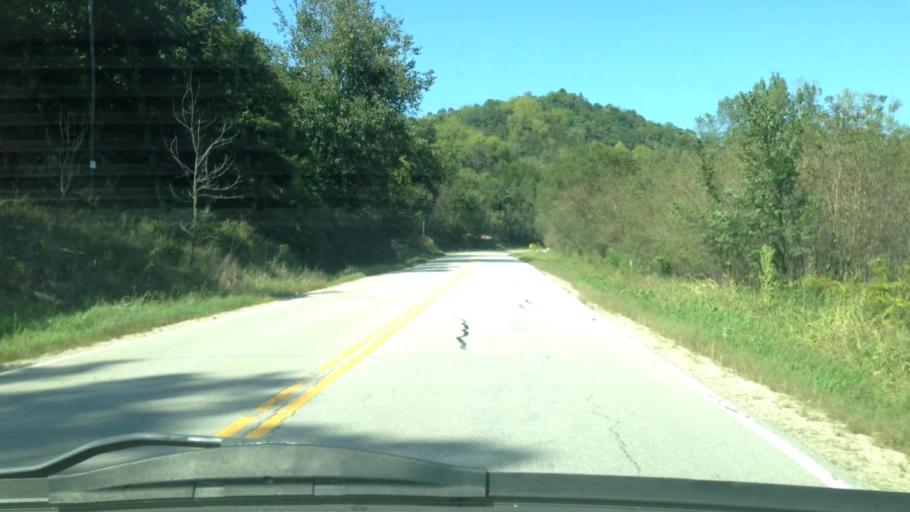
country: US
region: Minnesota
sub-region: Fillmore County
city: Rushford
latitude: 43.6721
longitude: -91.7929
